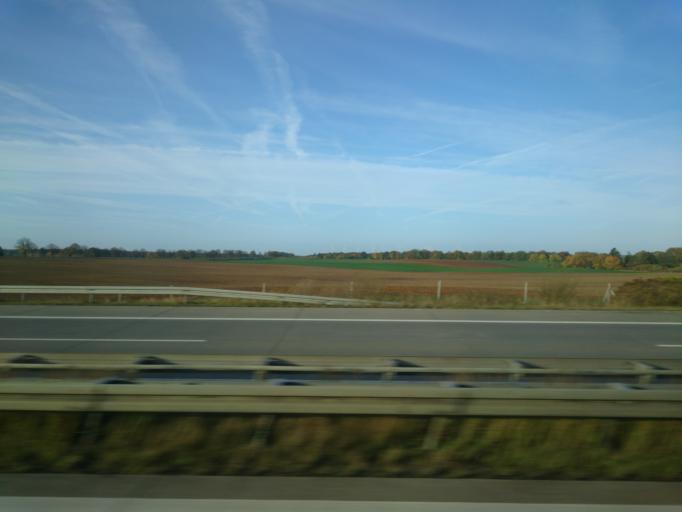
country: DE
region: Mecklenburg-Vorpommern
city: Dummerstorf
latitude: 53.9148
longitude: 12.2375
